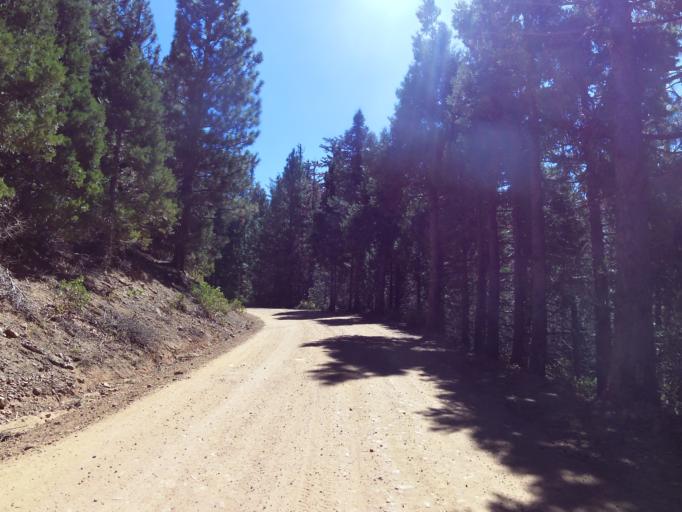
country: US
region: California
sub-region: Madera County
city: Oakhurst
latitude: 37.4401
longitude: -119.5368
